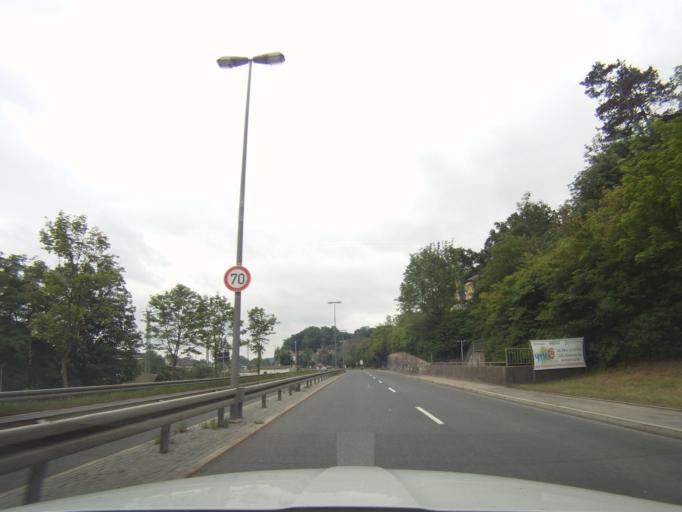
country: DE
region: Bavaria
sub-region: Upper Franconia
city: Coburg
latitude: 50.2665
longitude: 10.9558
